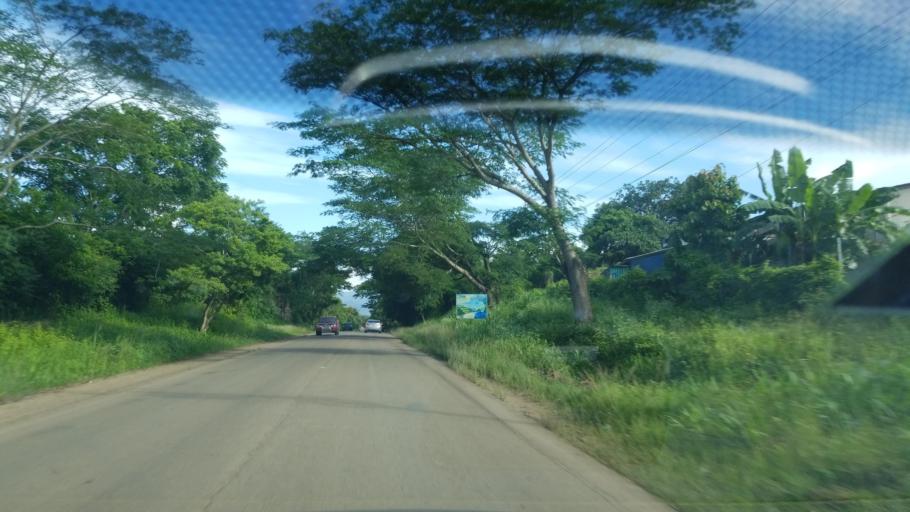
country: HN
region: El Paraiso
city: Arauli
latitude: 13.9487
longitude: -86.5602
